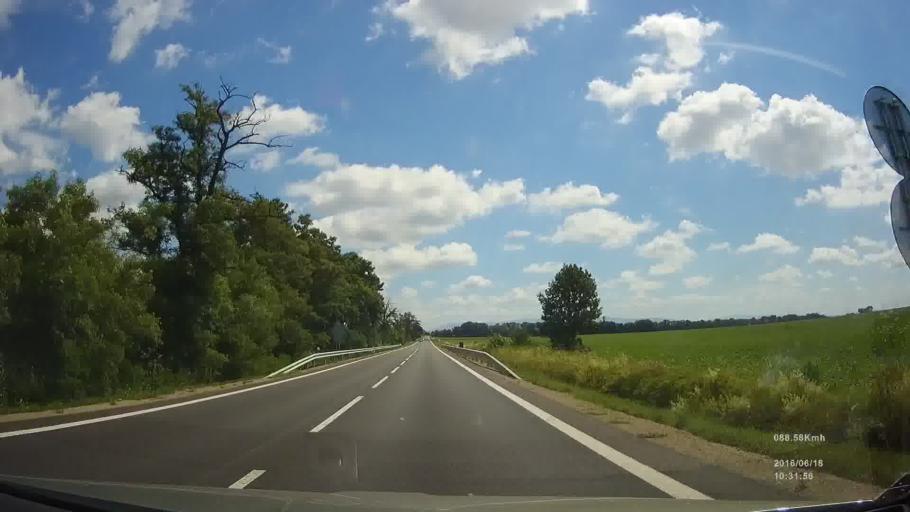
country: SK
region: Kosicky
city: Vinne
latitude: 48.7647
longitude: 22.0148
